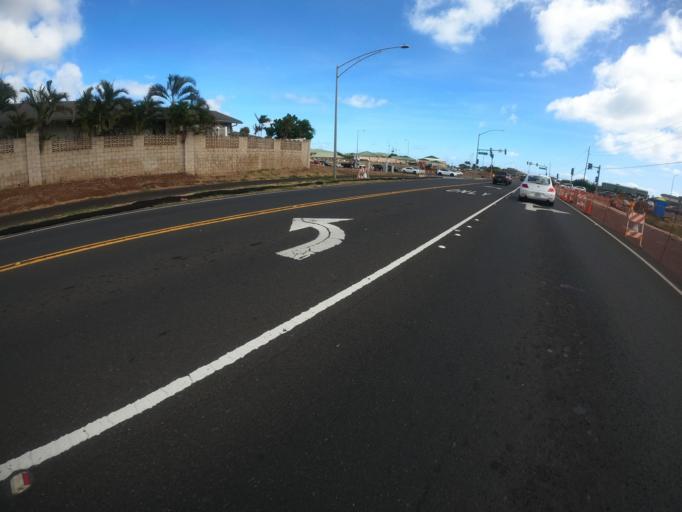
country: US
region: Hawaii
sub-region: Honolulu County
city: Makakilo City
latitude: 21.3301
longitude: -158.0722
